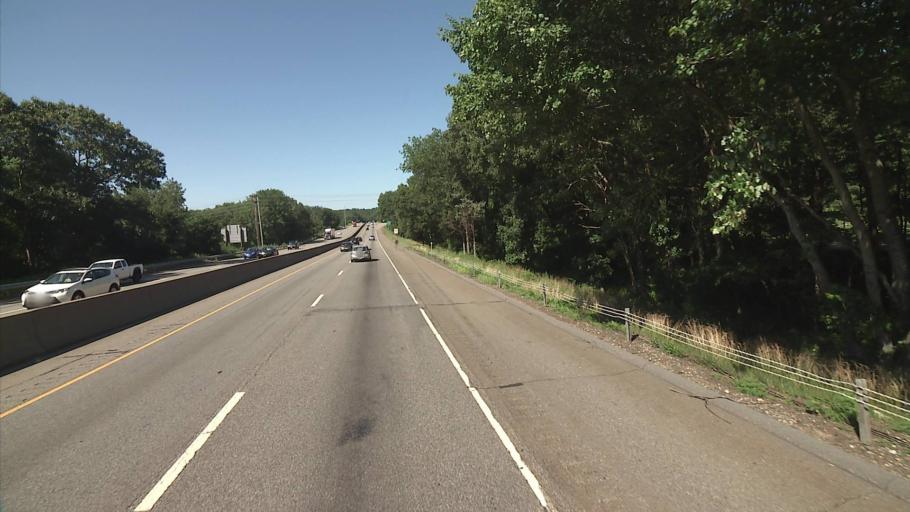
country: US
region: Connecticut
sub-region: Middlesex County
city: Old Saybrook
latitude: 41.3021
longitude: -72.3868
